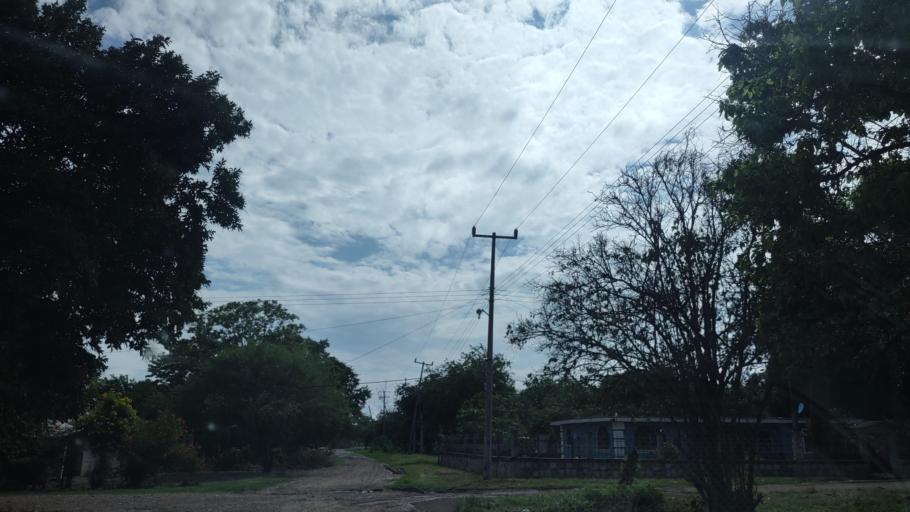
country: MX
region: Veracruz
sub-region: Panuco
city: Oviedo
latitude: 22.0011
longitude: -98.4566
